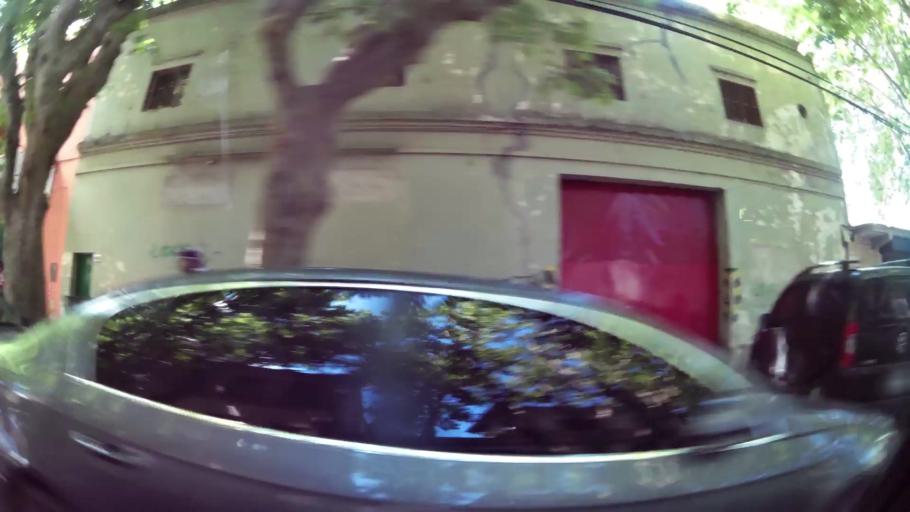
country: AR
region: Buenos Aires
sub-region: Partido de Tigre
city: Tigre
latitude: -34.4250
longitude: -58.5790
